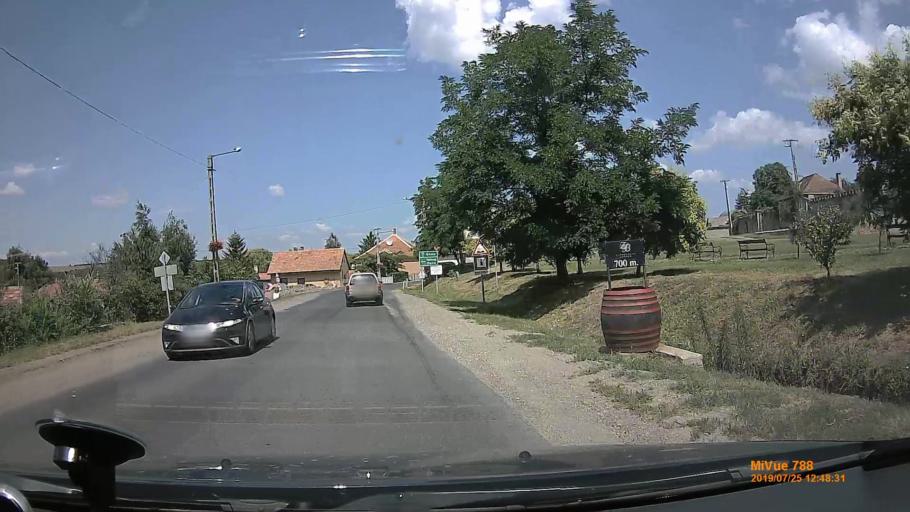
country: HU
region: Borsod-Abauj-Zemplen
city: Abaujszanto
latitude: 48.2696
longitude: 21.1835
